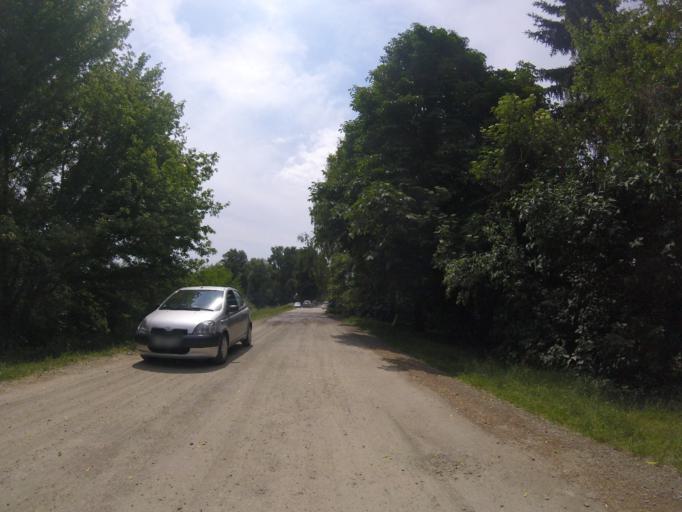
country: HU
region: Pest
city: Szodliget
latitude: 47.7150
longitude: 19.1218
